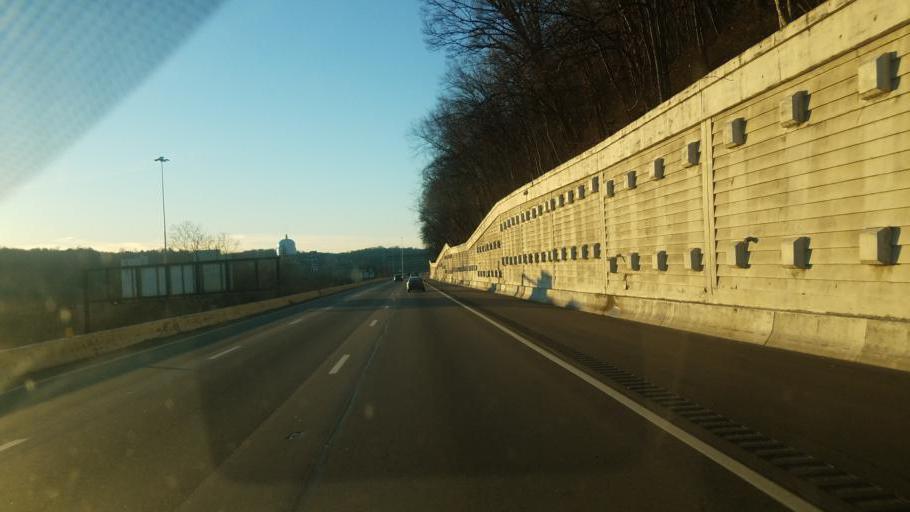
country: US
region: West Virginia
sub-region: Kanawha County
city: Charleston
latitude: 38.3345
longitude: -81.5991
